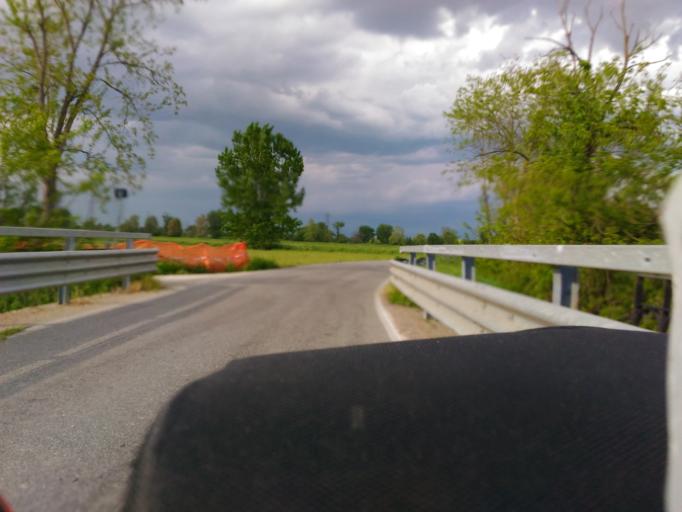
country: IT
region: Lombardy
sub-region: Citta metropolitana di Milano
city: Triginto
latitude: 45.4018
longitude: 9.3062
